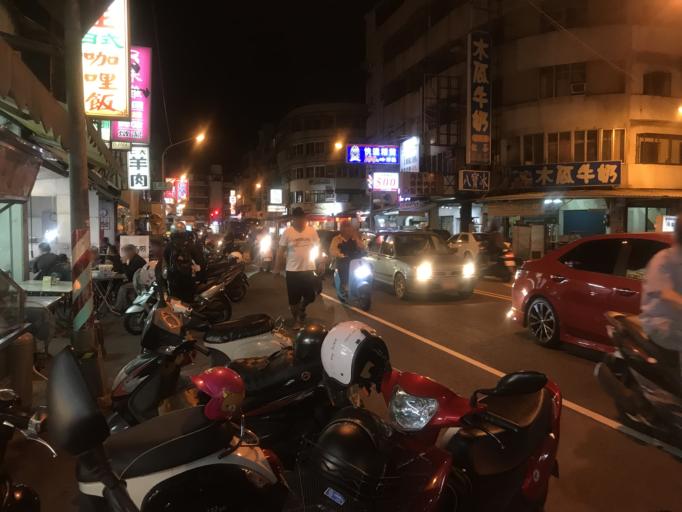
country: TW
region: Kaohsiung
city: Kaohsiung
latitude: 22.6347
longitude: 120.3269
